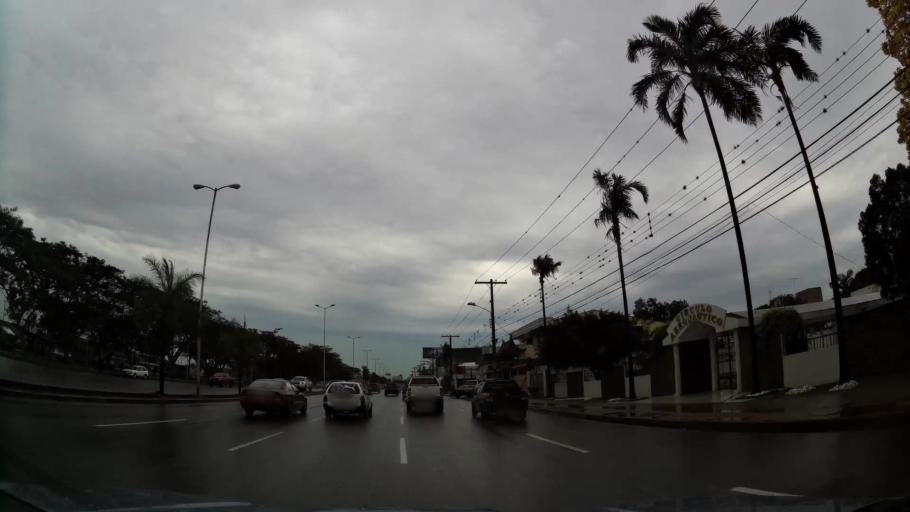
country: BO
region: Santa Cruz
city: Santa Cruz de la Sierra
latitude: -17.7983
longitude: -63.1768
